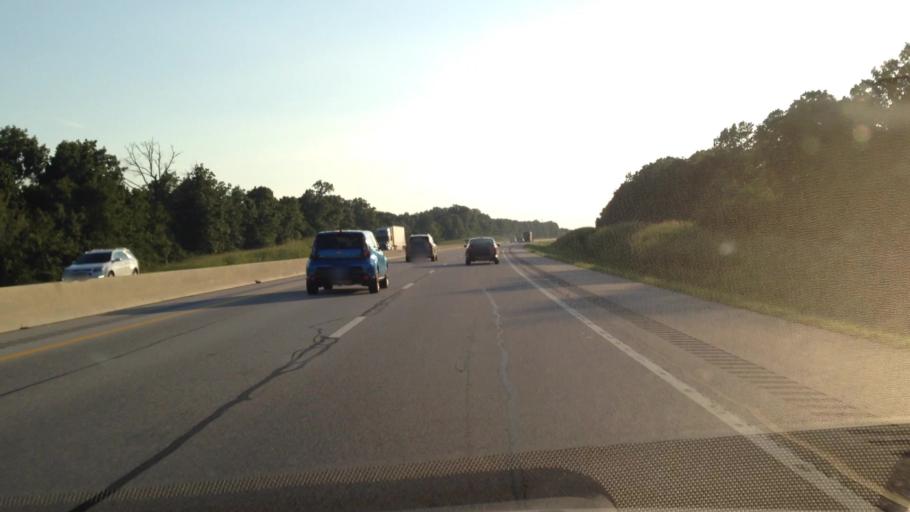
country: US
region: Kansas
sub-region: Cherokee County
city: Baxter Springs
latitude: 36.9418
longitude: -94.6884
